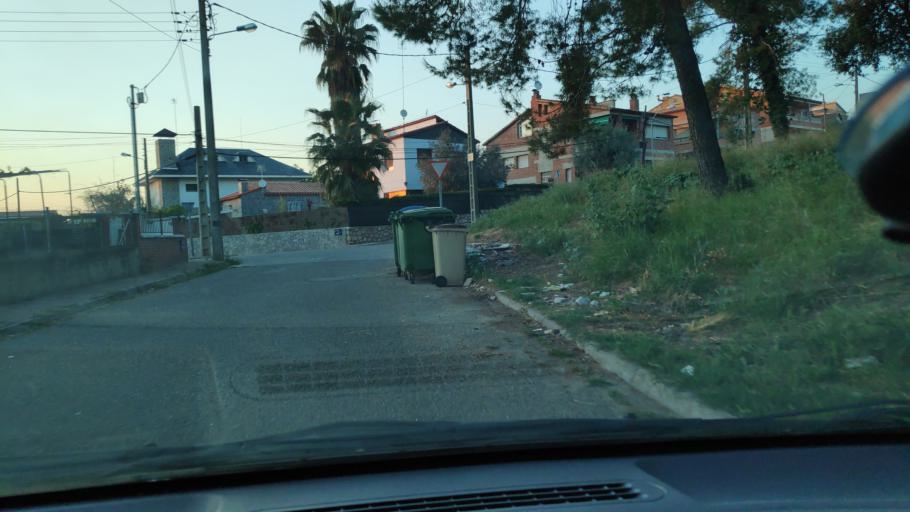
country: ES
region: Catalonia
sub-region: Provincia de Barcelona
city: Sant Quirze del Valles
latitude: 41.5321
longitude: 2.0467
